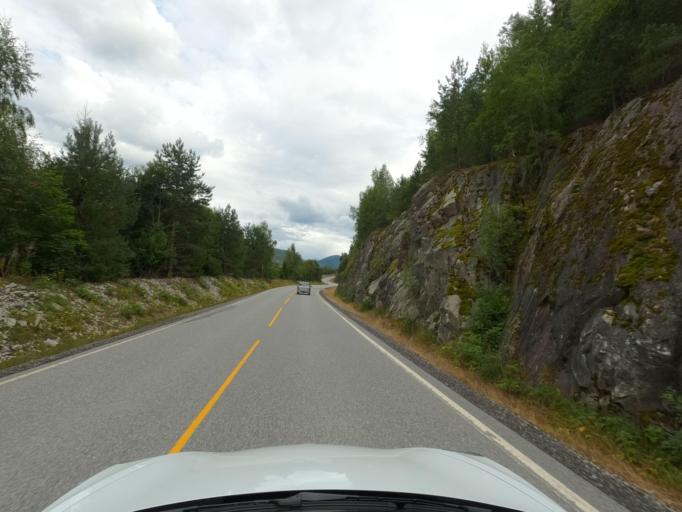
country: NO
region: Telemark
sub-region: Hjartdal
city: Sauland
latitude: 59.8024
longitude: 8.9944
